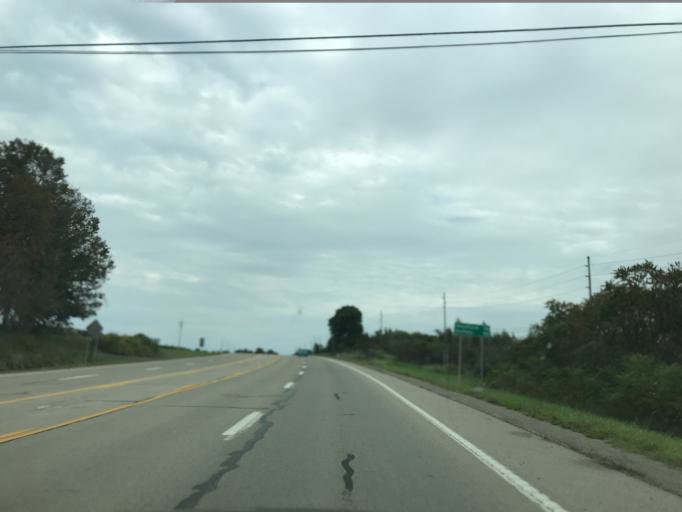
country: US
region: Pennsylvania
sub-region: Erie County
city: North East
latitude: 42.2196
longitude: -79.8213
